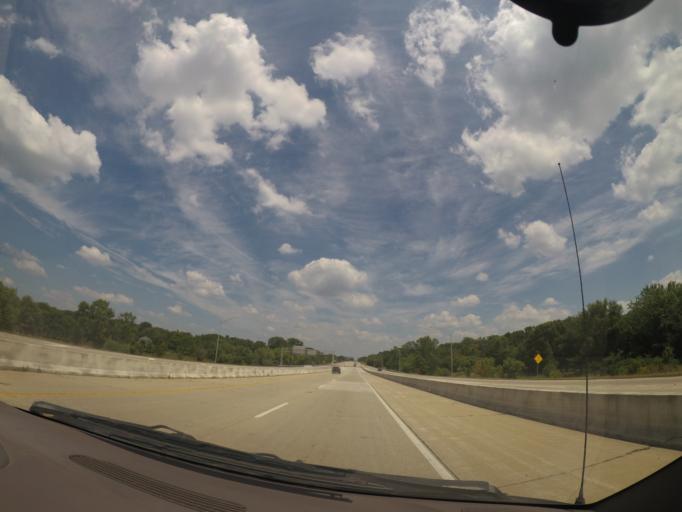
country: US
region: Indiana
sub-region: Elkhart County
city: Dunlap
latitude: 41.6668
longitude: -85.8828
